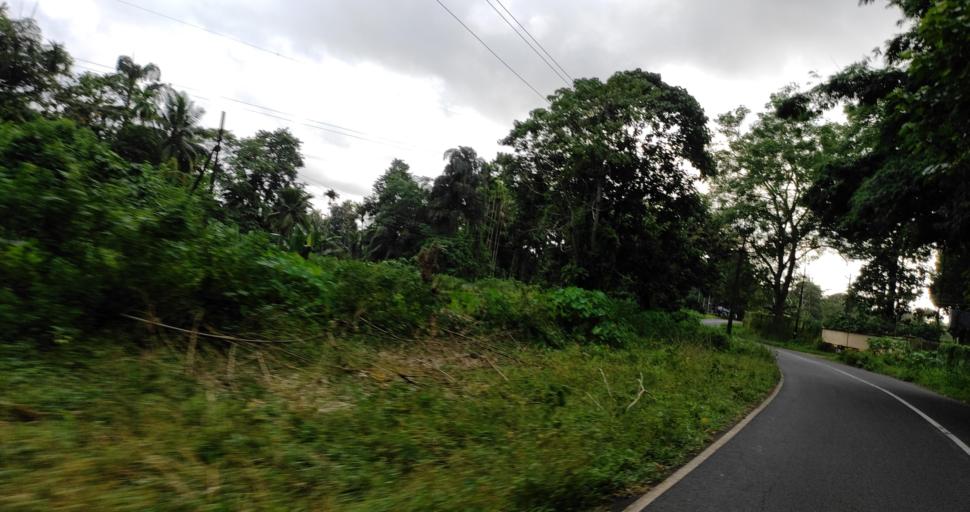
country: IN
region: Kerala
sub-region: Thrissur District
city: Kizhake Chalakudi
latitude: 10.2996
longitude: 76.4378
